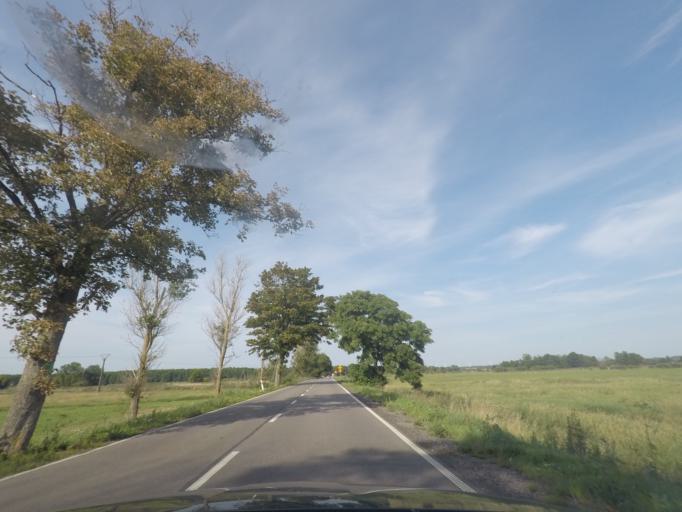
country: PL
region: Pomeranian Voivodeship
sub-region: Powiat leborski
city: Leba
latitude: 54.6526
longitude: 17.5606
